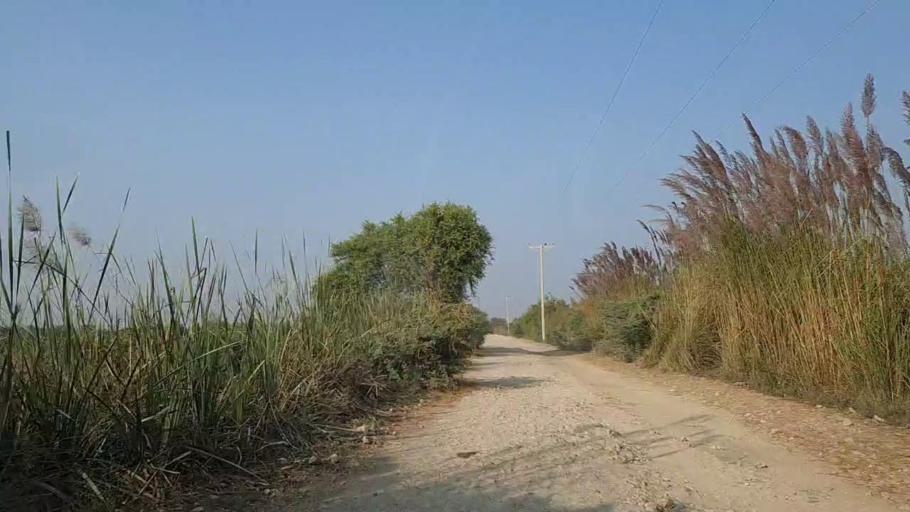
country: PK
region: Sindh
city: Mirpur Sakro
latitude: 24.6300
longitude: 67.7465
